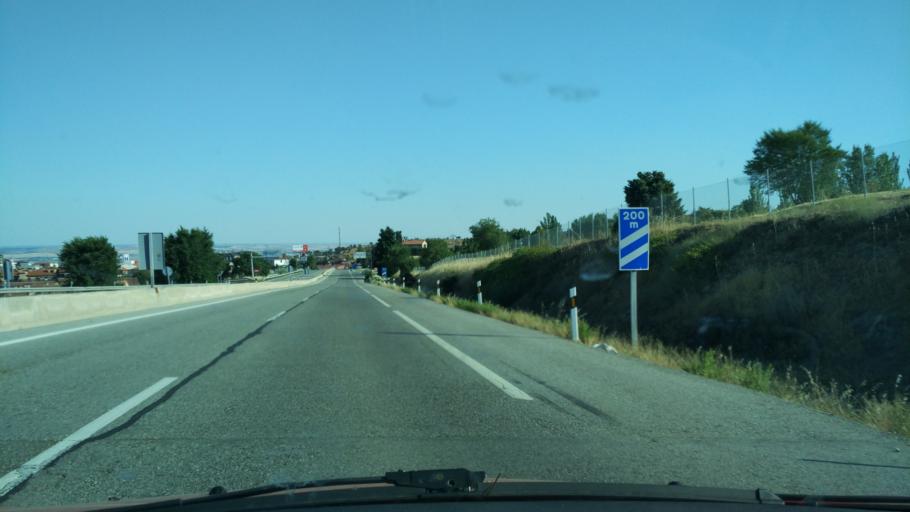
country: ES
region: Madrid
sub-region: Provincia de Madrid
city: Pedrezuela
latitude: 40.7411
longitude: -3.5880
